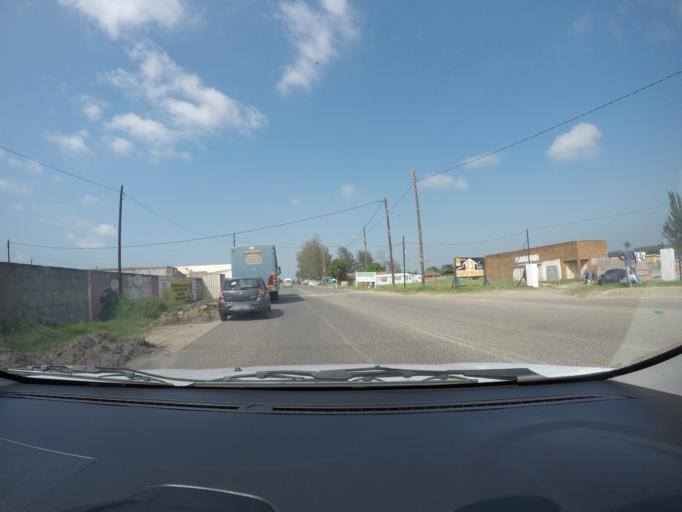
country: ZA
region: KwaZulu-Natal
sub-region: uThungulu District Municipality
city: eSikhawini
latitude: -28.8894
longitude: 31.8945
